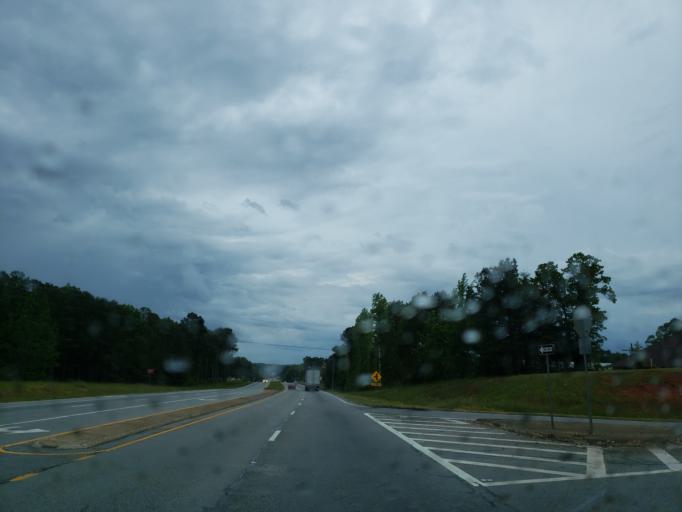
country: US
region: Georgia
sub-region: Haralson County
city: Buchanan
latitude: 33.7719
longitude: -85.1713
